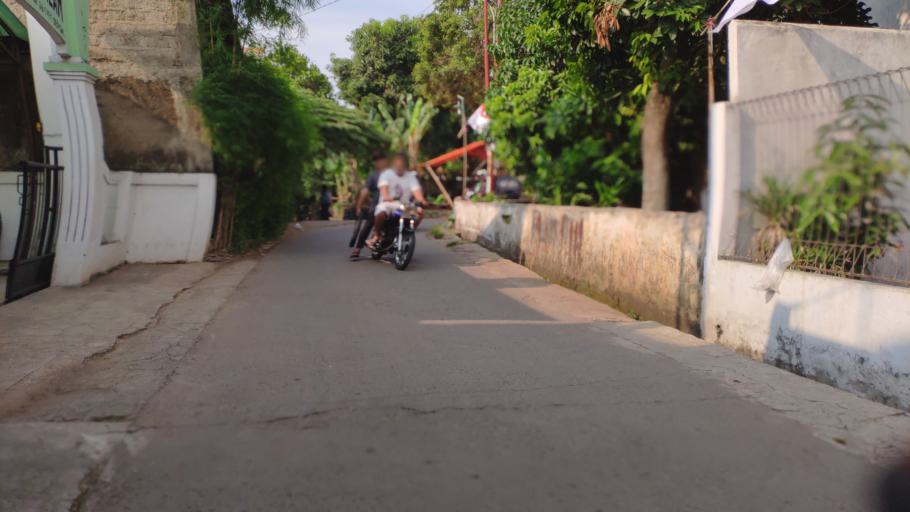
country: ID
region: West Java
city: Pamulang
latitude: -6.3258
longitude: 106.7932
